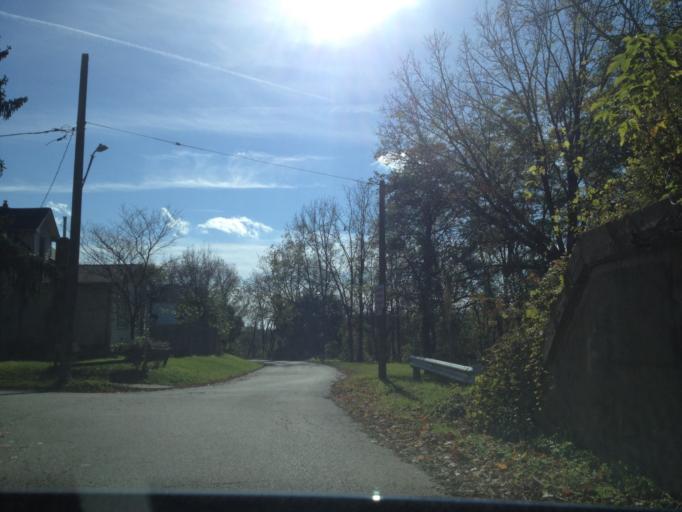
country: CA
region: Ontario
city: St. Thomas
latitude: 42.7782
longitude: -81.2095
